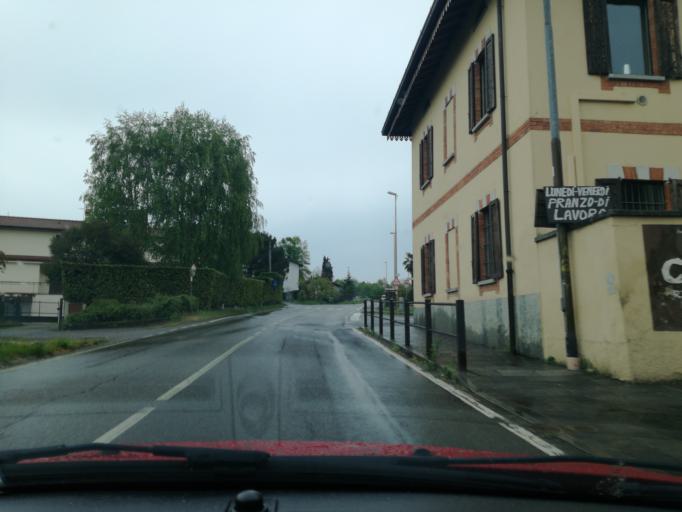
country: IT
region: Lombardy
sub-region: Provincia di Monza e Brianza
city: Tregasio
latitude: 45.6921
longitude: 9.2829
